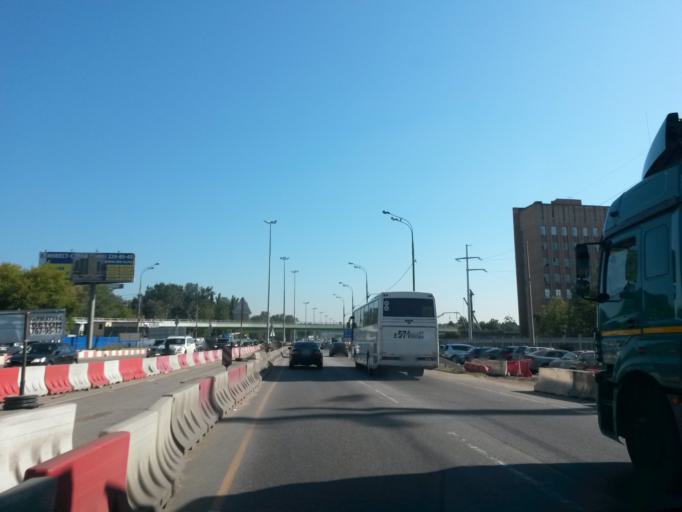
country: RU
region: Moskovskaya
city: Korolev
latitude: 55.9293
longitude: 37.8028
